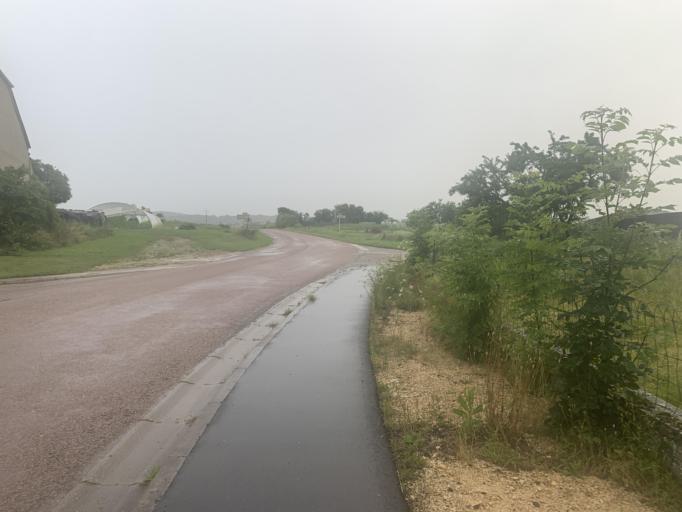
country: FR
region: Lorraine
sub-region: Departement des Vosges
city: Chatenois
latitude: 48.2872
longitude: 5.8480
